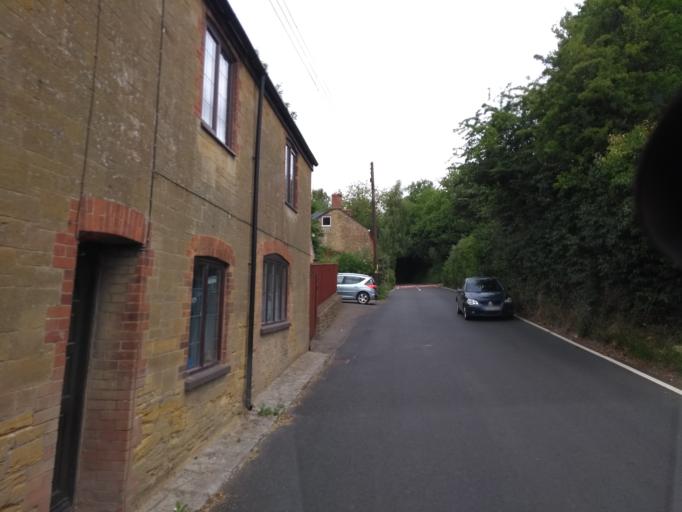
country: GB
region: England
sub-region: Somerset
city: South Petherton
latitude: 50.9271
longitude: -2.8194
